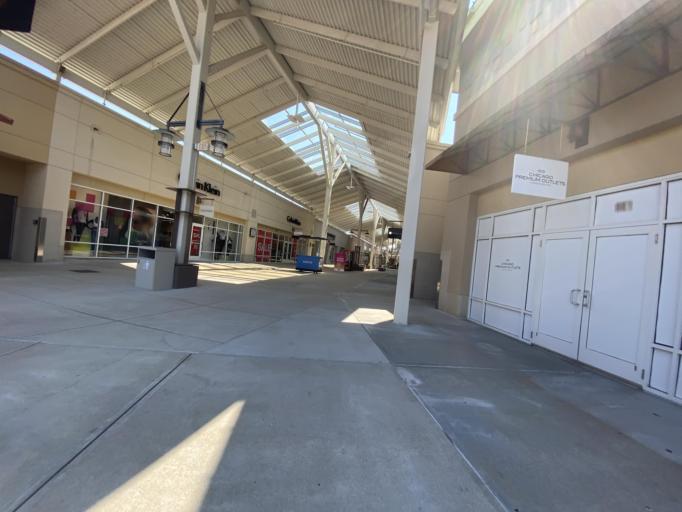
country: US
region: Illinois
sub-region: Kane County
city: North Aurora
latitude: 41.8002
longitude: -88.2753
